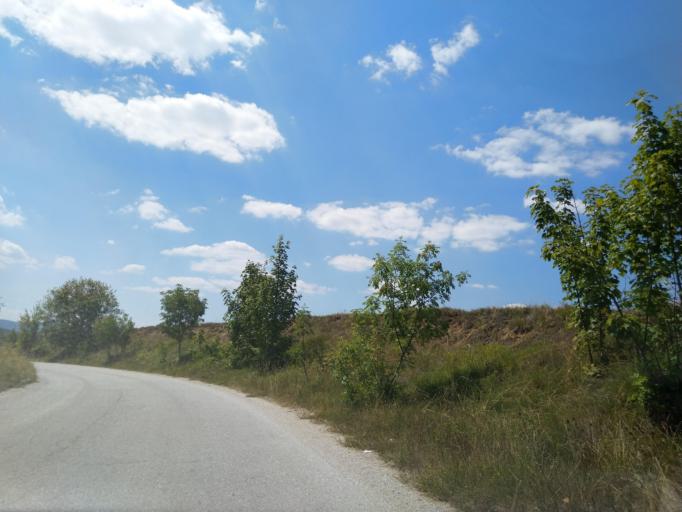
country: RS
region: Central Serbia
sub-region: Zlatiborski Okrug
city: Nova Varos
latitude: 43.4284
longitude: 19.9394
